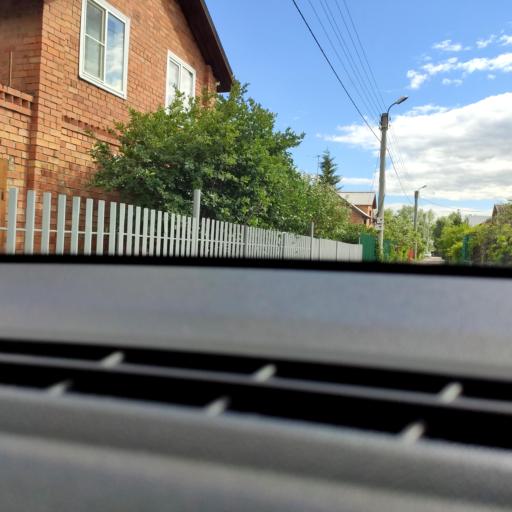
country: RU
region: Samara
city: Podstepki
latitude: 53.5819
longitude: 49.0677
